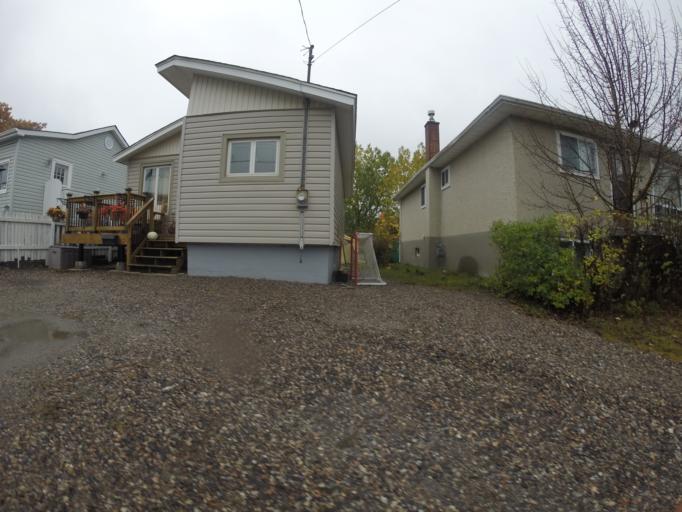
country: CA
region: Ontario
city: Greater Sudbury
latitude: 46.4744
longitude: -81.0299
